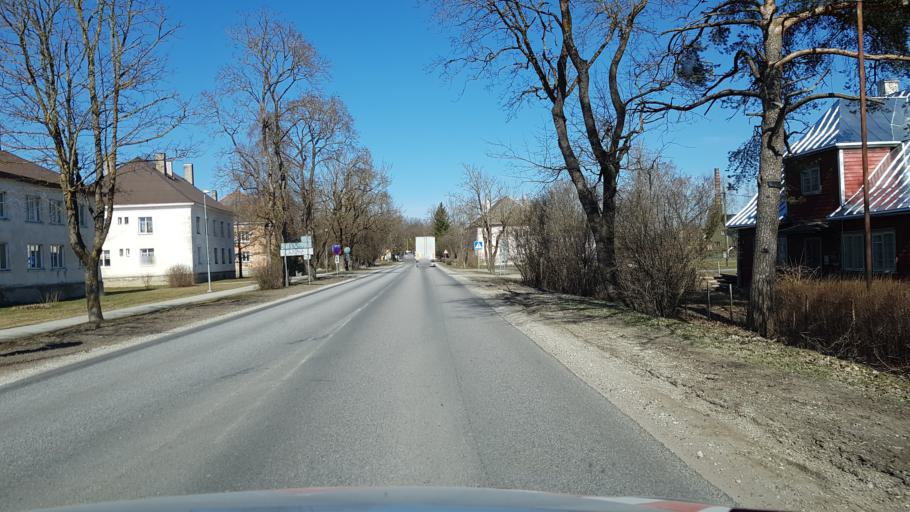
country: EE
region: Laeaene-Virumaa
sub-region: Vaeike-Maarja vald
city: Vaike-Maarja
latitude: 59.1300
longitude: 26.2527
